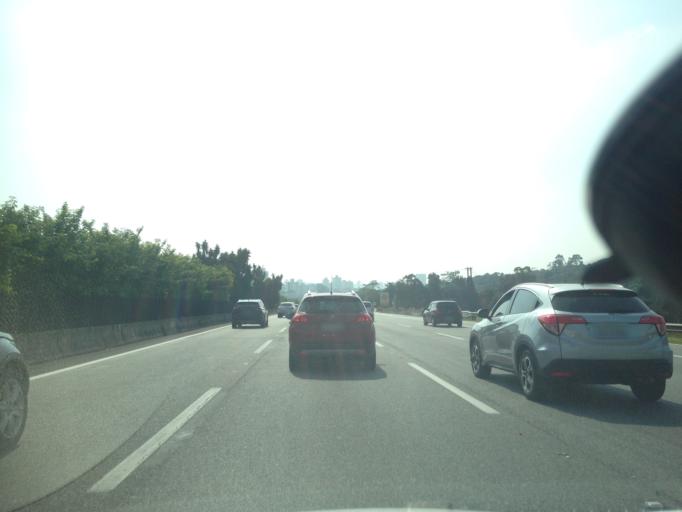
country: BR
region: Sao Paulo
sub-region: Diadema
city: Diadema
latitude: -23.6621
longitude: -46.6332
